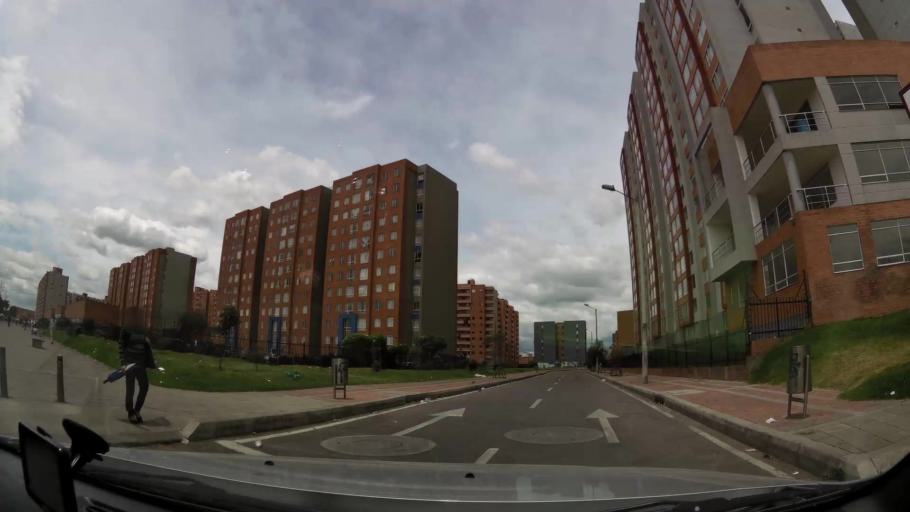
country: CO
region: Bogota D.C.
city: Bogota
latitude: 4.6369
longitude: -74.1540
